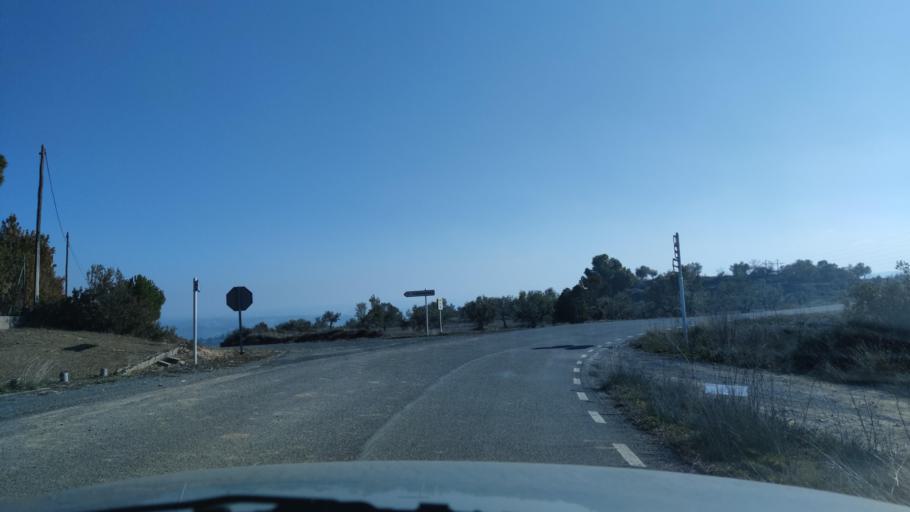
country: ES
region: Catalonia
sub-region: Provincia de Lleida
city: Torrebesses
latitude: 41.4358
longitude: 0.5672
